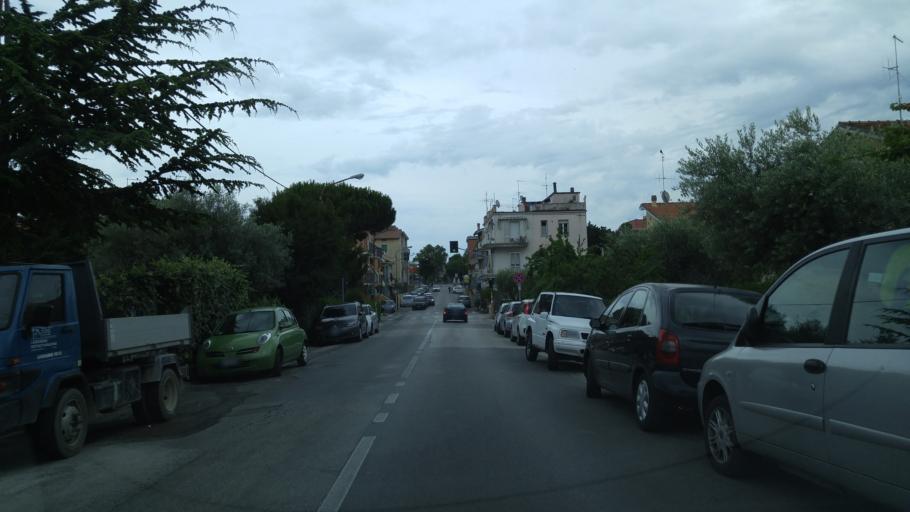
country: IT
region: The Marches
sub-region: Provincia di Pesaro e Urbino
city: Pesaro
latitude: 43.9173
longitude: 12.9002
